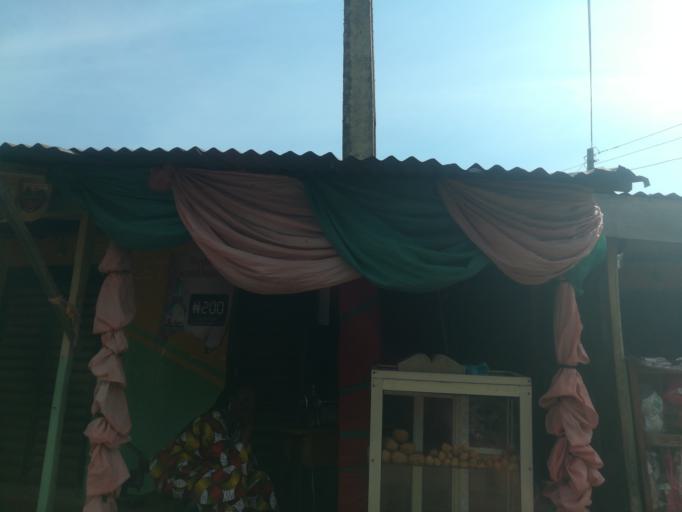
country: NG
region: Oyo
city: Ibadan
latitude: 7.3899
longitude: 3.8205
